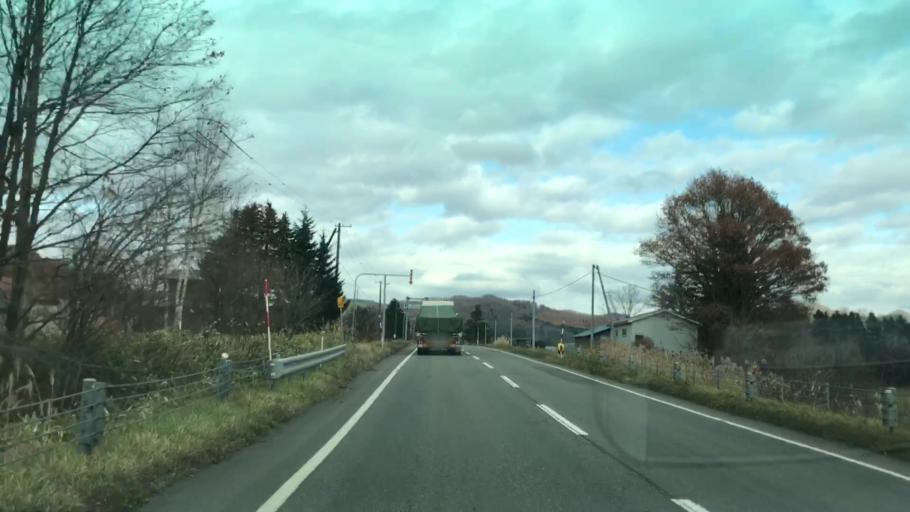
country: JP
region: Hokkaido
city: Shimo-furano
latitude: 42.8698
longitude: 142.4270
